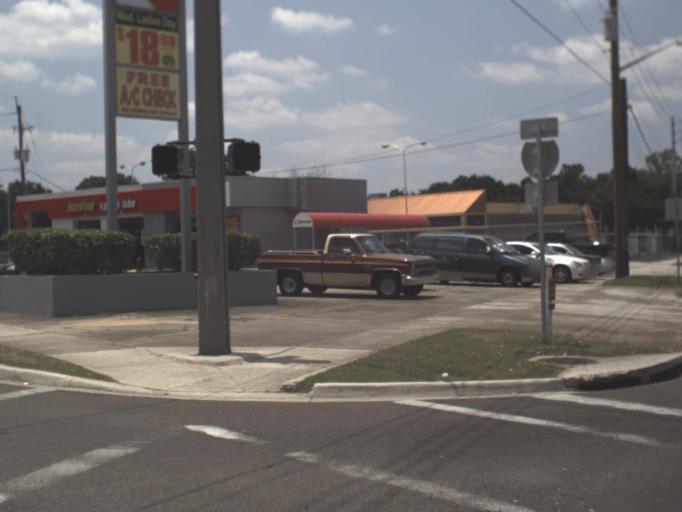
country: US
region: Florida
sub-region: Duval County
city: Jacksonville
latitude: 30.3152
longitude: -81.7308
